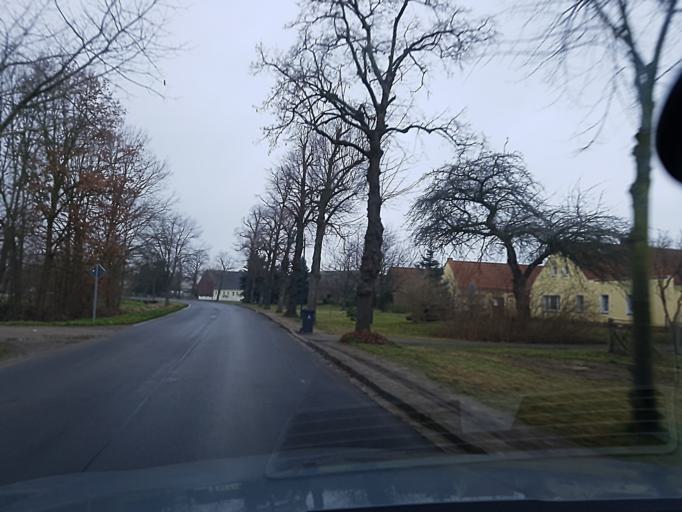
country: DE
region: Brandenburg
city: Doberlug-Kirchhain
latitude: 51.6519
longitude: 13.5471
